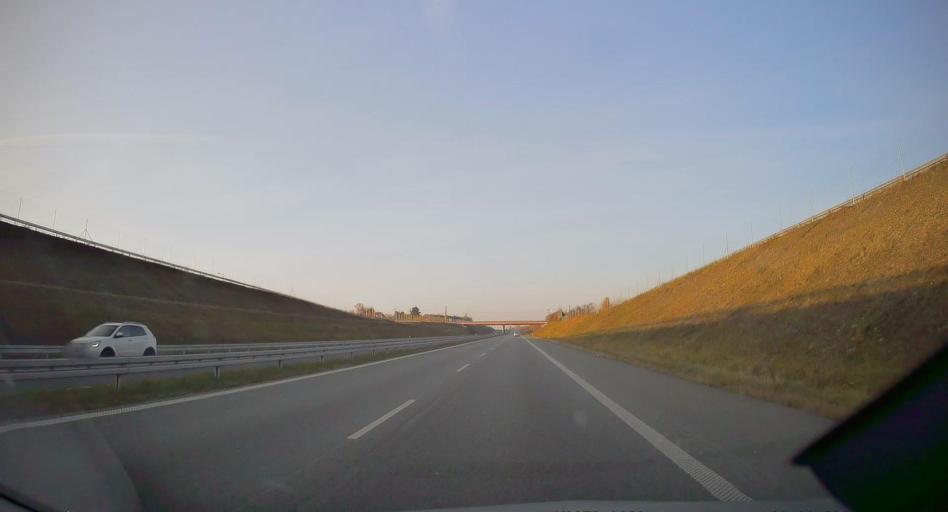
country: PL
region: Silesian Voivodeship
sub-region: Powiat bedzinski
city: Mierzecice
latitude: 50.4355
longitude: 19.1492
